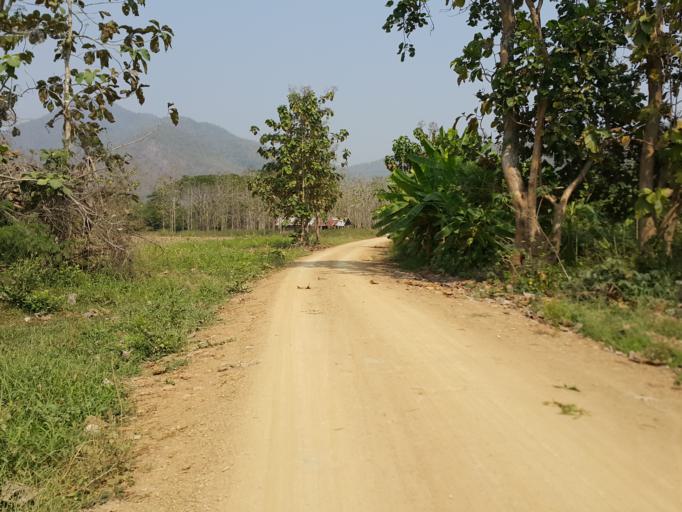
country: TH
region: Sukhothai
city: Thung Saliam
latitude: 17.3394
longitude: 99.4646
